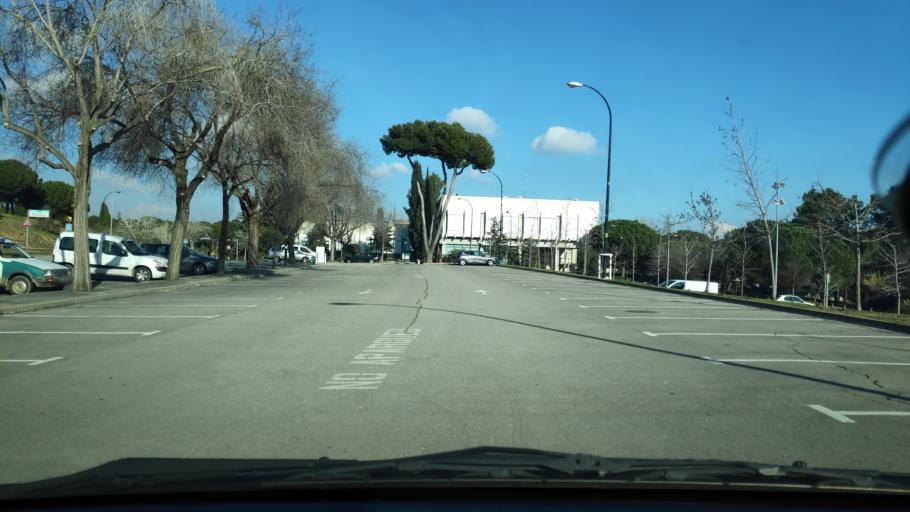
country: ES
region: Catalonia
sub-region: Provincia de Barcelona
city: Barbera del Valles
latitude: 41.5029
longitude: 2.0991
